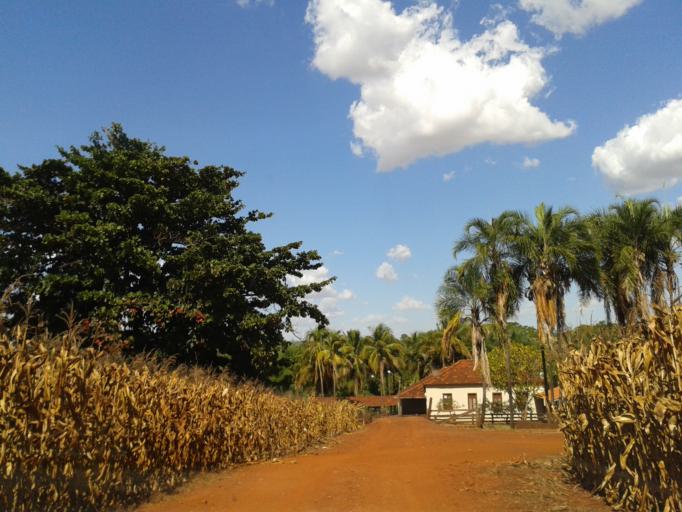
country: BR
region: Minas Gerais
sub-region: Capinopolis
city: Capinopolis
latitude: -18.6278
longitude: -49.4752
